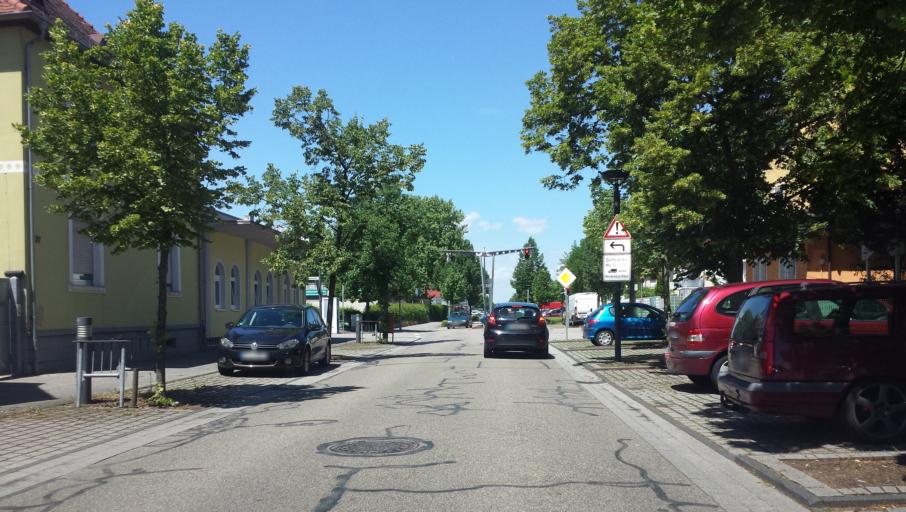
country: DE
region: Baden-Wuerttemberg
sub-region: Karlsruhe Region
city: Waghausel
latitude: 49.2291
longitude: 8.5160
